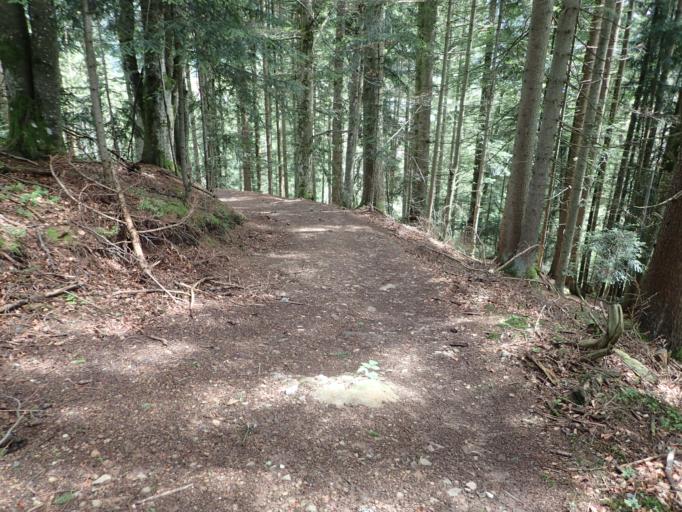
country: AT
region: Salzburg
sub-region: Politischer Bezirk Sankt Johann im Pongau
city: Wagrain
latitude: 47.3390
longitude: 13.2984
